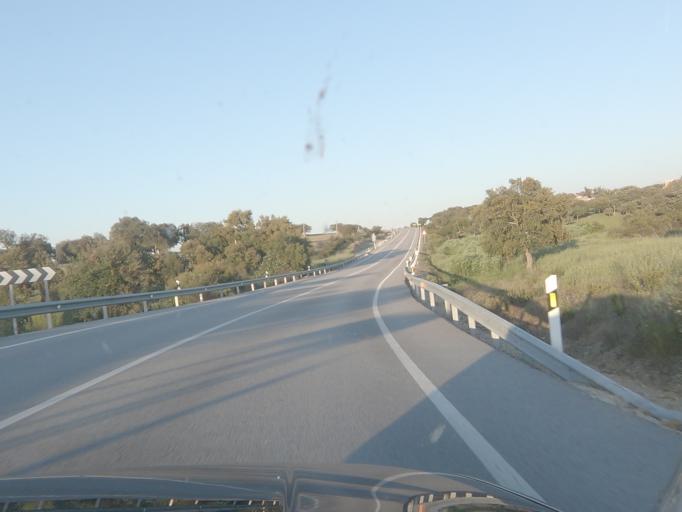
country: ES
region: Extremadura
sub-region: Provincia de Caceres
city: Carbajo
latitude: 39.4984
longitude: -7.1820
